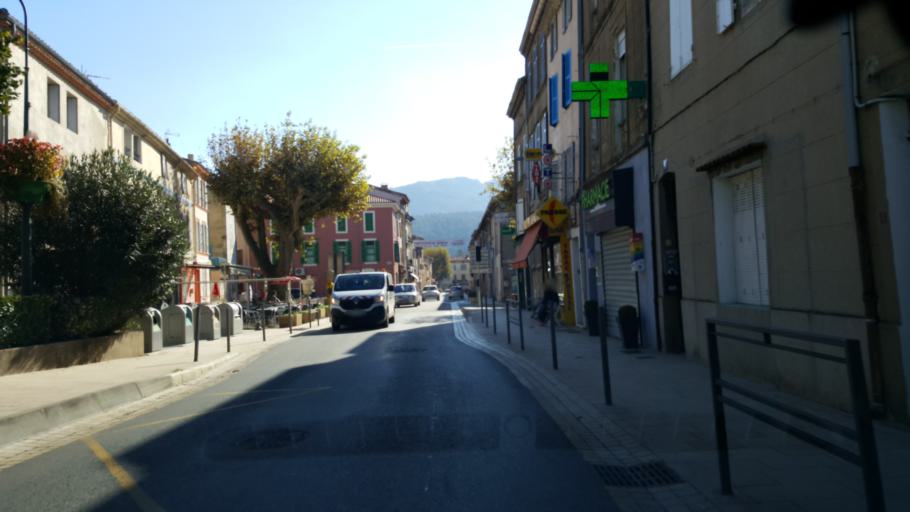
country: FR
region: Provence-Alpes-Cote d'Azur
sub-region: Departement du Var
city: Saint-Zacharie
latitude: 43.3845
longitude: 5.7067
